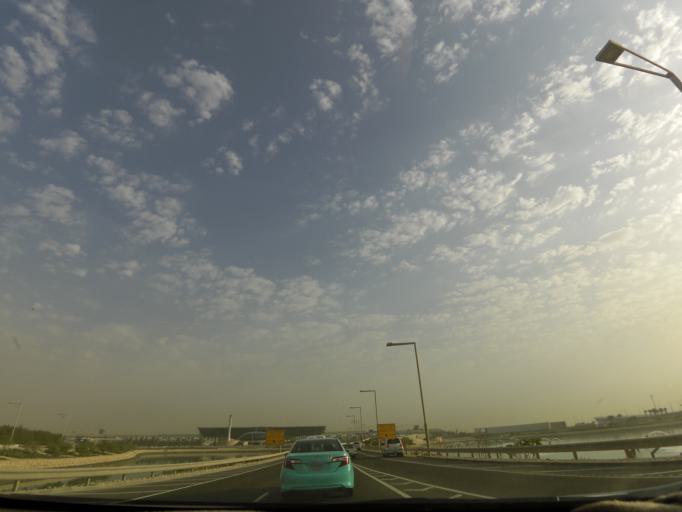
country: QA
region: Al Wakrah
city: Al Wakrah
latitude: 25.2534
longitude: 51.6173
